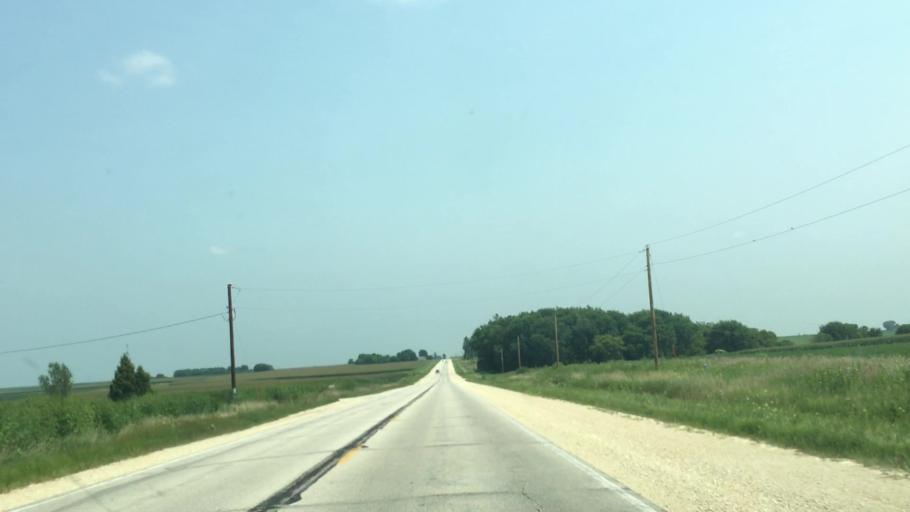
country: US
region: Iowa
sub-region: Fayette County
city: Oelwein
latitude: 42.6799
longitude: -91.8514
